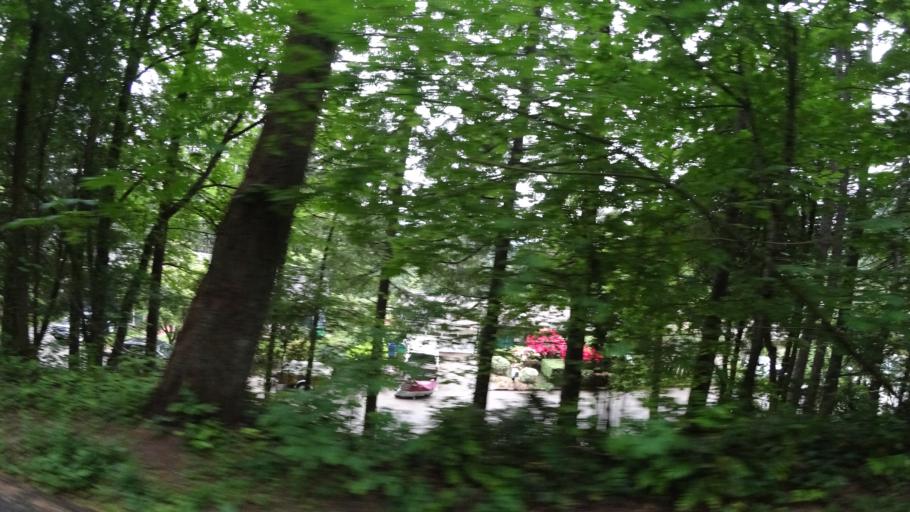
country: US
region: Oregon
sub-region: Multnomah County
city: Portland
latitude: 45.4858
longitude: -122.6959
